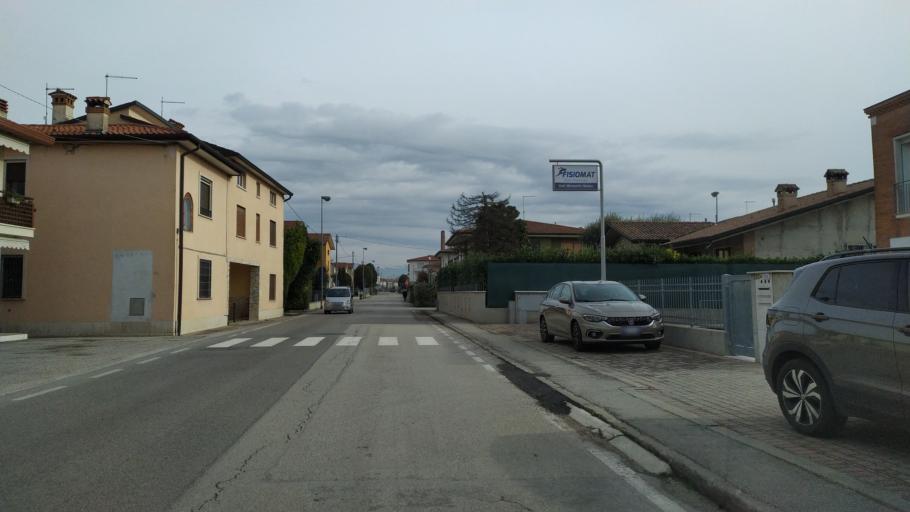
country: IT
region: Veneto
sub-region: Provincia di Vicenza
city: Villaverla
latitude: 45.6528
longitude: 11.4886
